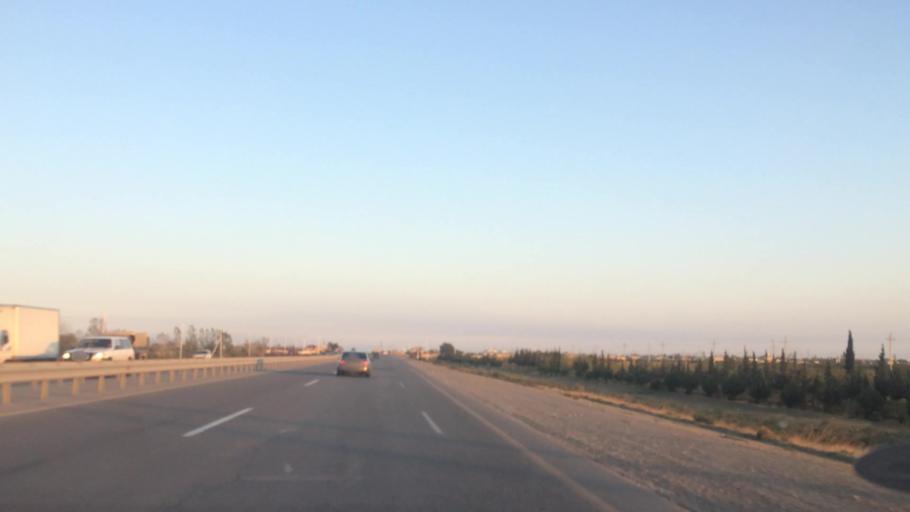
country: AZ
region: Baki
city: Qobustan
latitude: 39.9755
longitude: 49.2500
